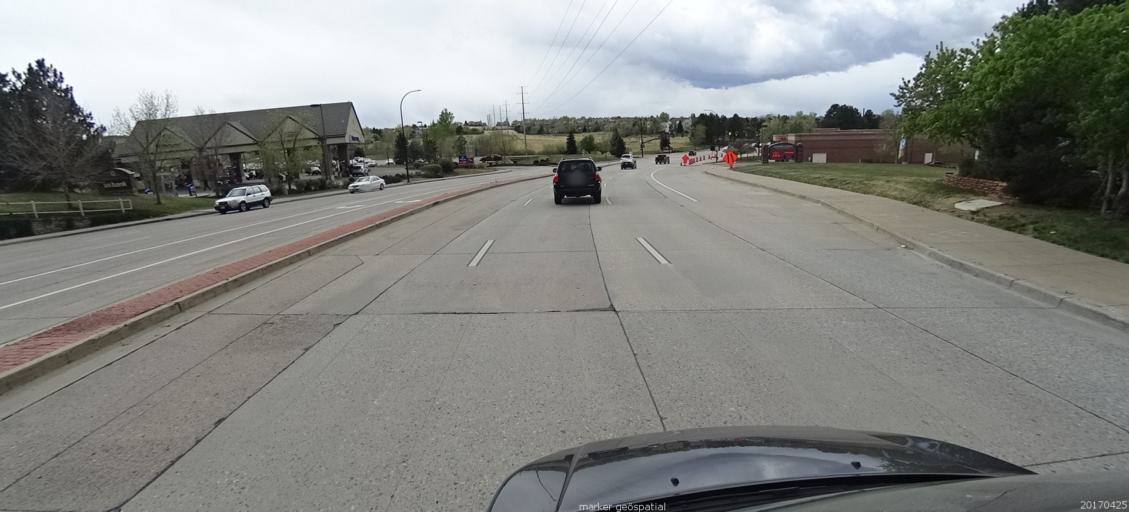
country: US
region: Colorado
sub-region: Douglas County
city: Acres Green
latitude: 39.5603
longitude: -104.9046
